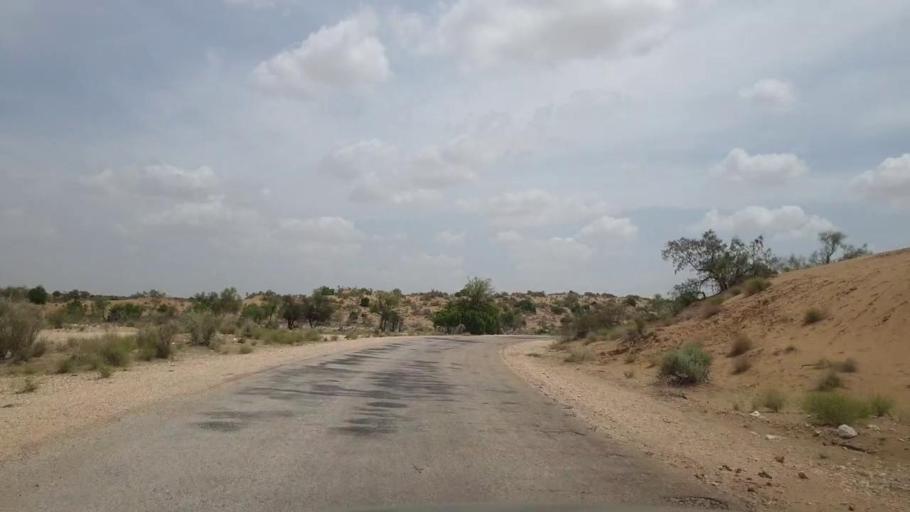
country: PK
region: Sindh
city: Kot Diji
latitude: 27.1648
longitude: 69.2229
